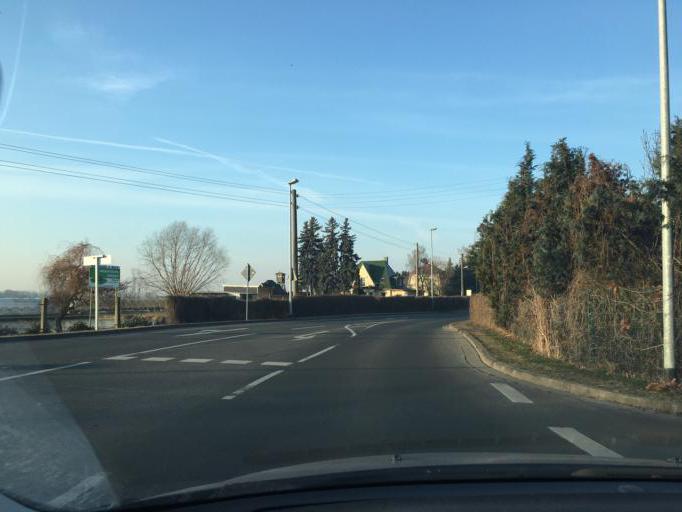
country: DE
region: Saxony
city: Borsdorf
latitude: 51.3389
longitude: 12.5165
